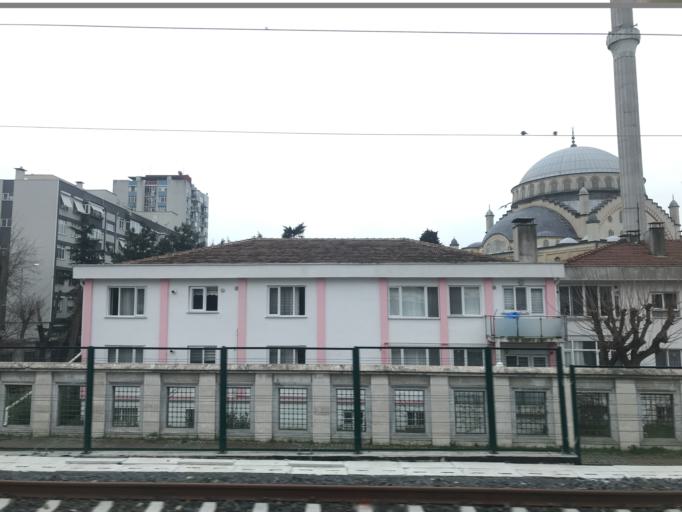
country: TR
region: Istanbul
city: Bahcelievler
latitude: 40.9800
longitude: 28.8593
